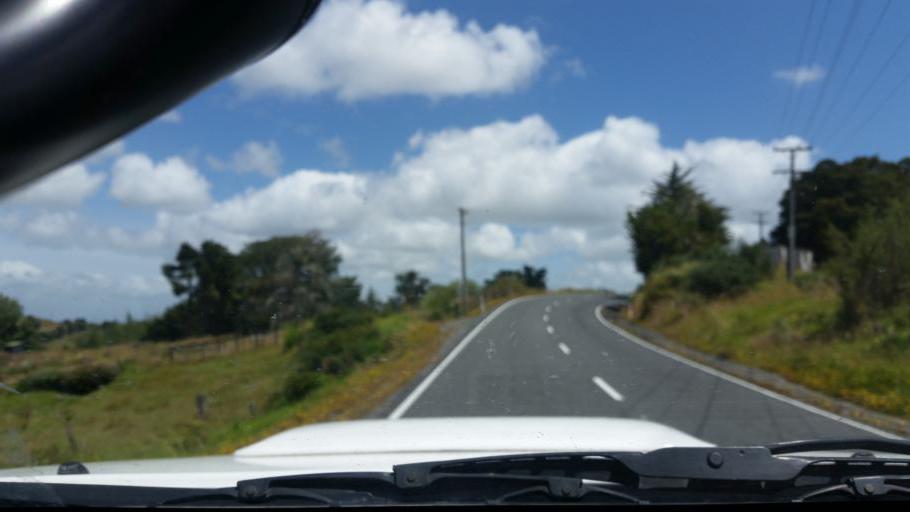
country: NZ
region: Northland
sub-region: Whangarei
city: Ruakaka
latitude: -36.0617
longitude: 174.2716
